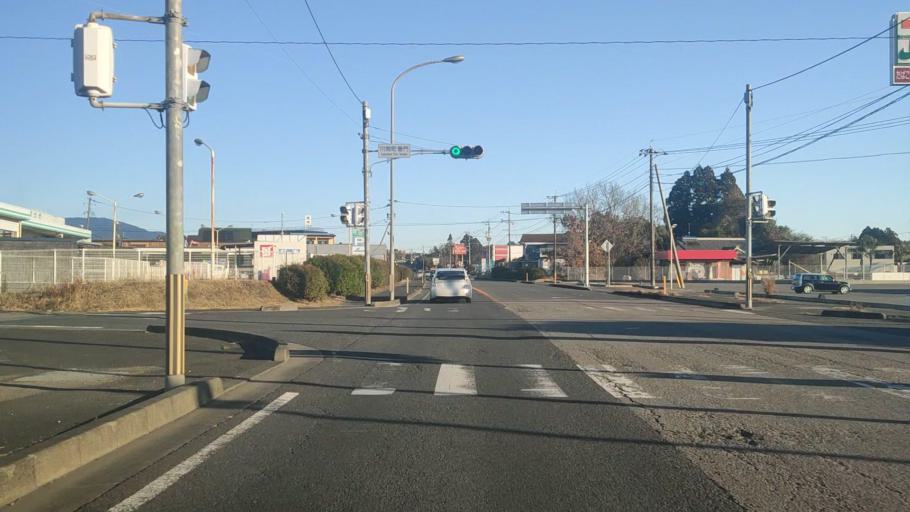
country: JP
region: Miyazaki
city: Takanabe
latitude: 32.1871
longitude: 131.5235
